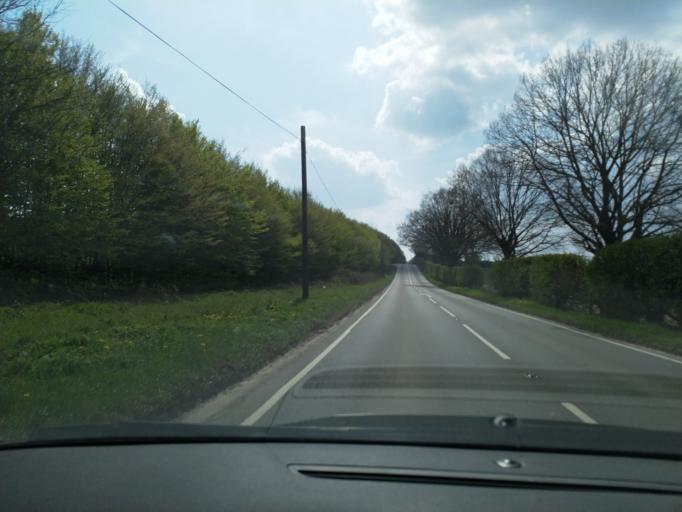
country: GB
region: England
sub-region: Warwickshire
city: Royal Leamington Spa
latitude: 52.3238
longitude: -1.5102
